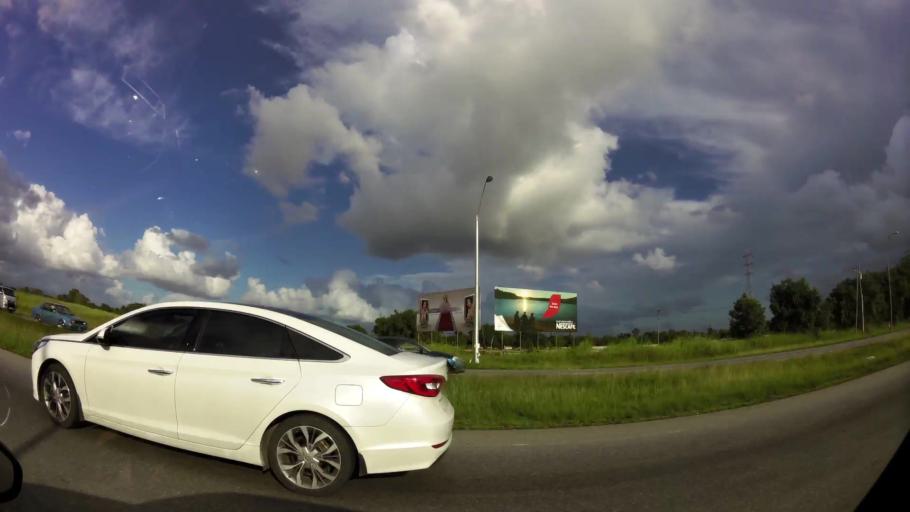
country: TT
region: Chaguanas
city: Chaguanas
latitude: 10.4856
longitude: -61.4057
